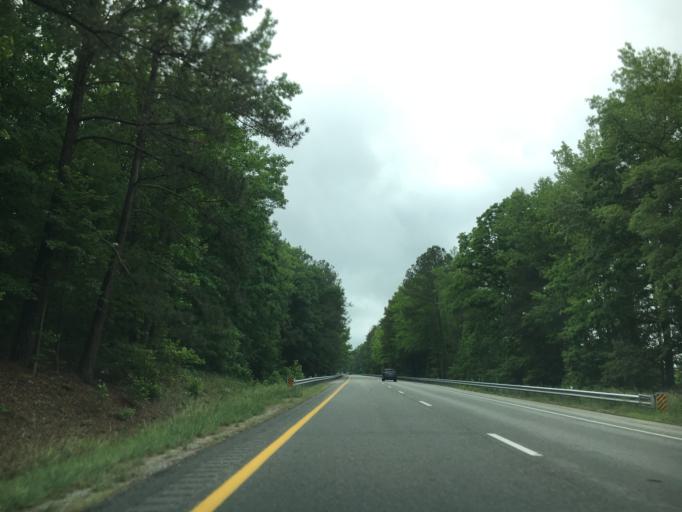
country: US
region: Virginia
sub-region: Brunswick County
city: Lawrenceville
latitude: 36.9021
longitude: -77.7933
